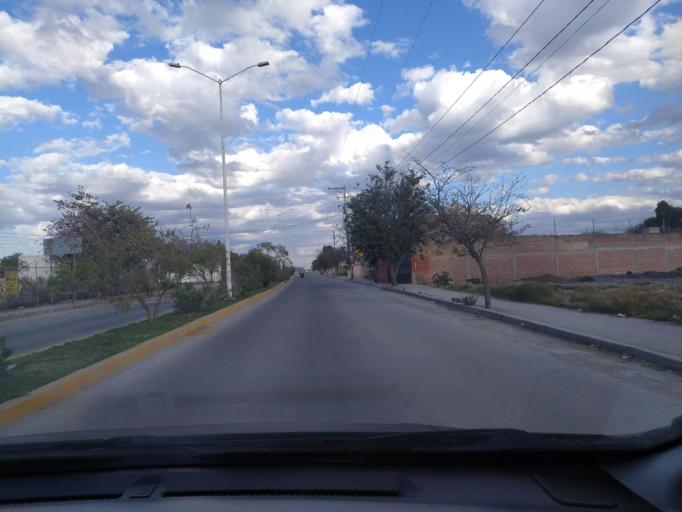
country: LA
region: Oudomxai
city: Muang La
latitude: 21.0175
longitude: 101.8410
